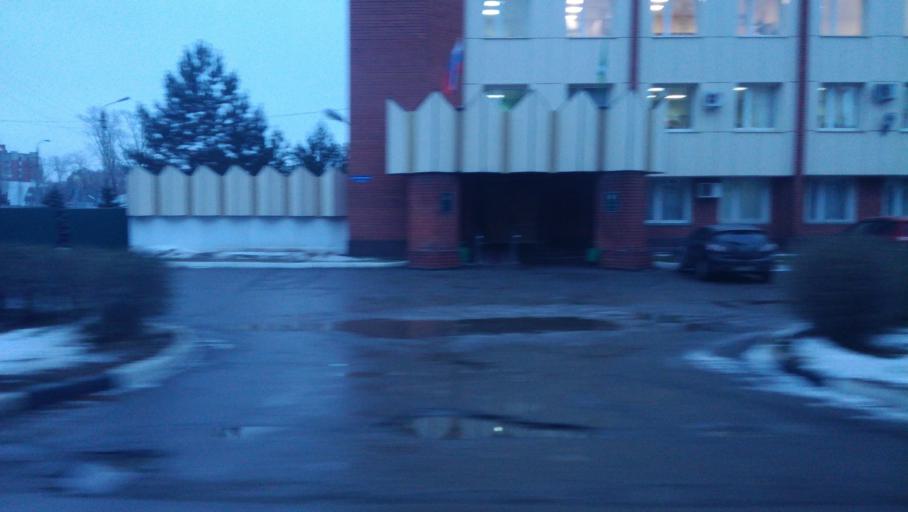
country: RU
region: Tula
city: Tula
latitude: 54.1972
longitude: 37.5771
